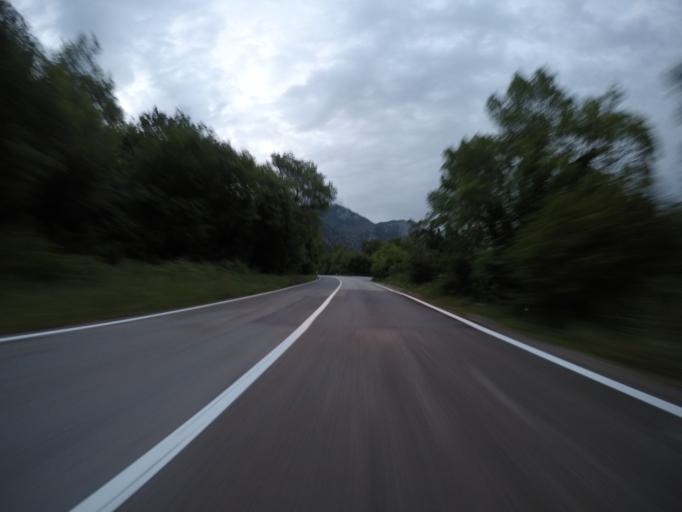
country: ME
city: Petrovac na Moru
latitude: 42.1972
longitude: 18.9708
